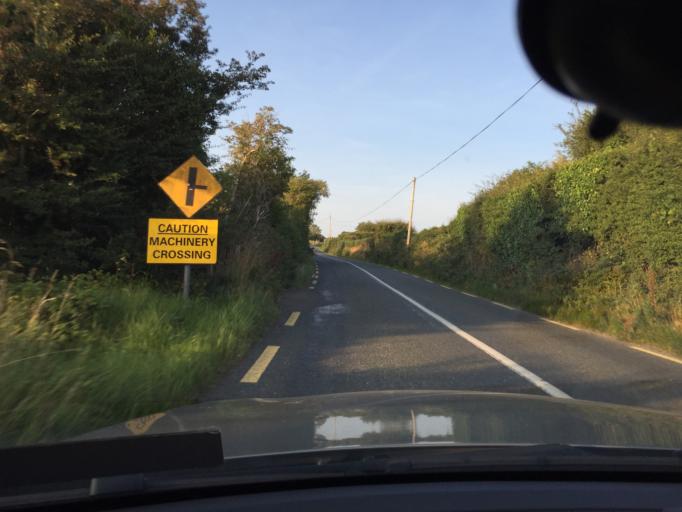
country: IE
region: Leinster
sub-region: Wicklow
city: Rathdrum
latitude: 53.0504
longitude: -6.2388
